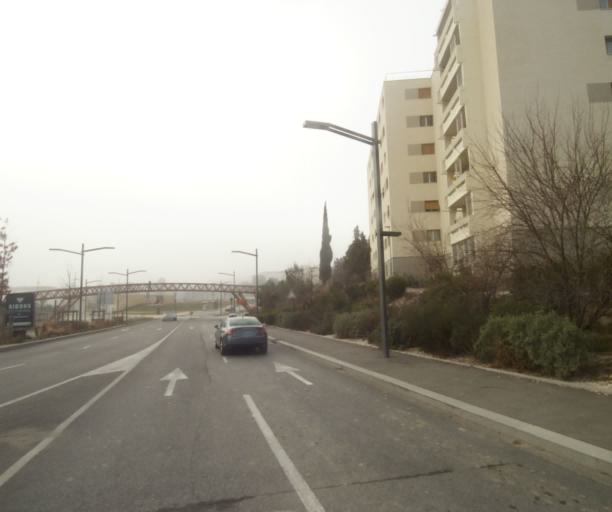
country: FR
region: Provence-Alpes-Cote d'Azur
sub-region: Departement des Bouches-du-Rhone
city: Aix-en-Provence
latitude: 43.5321
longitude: 5.4161
